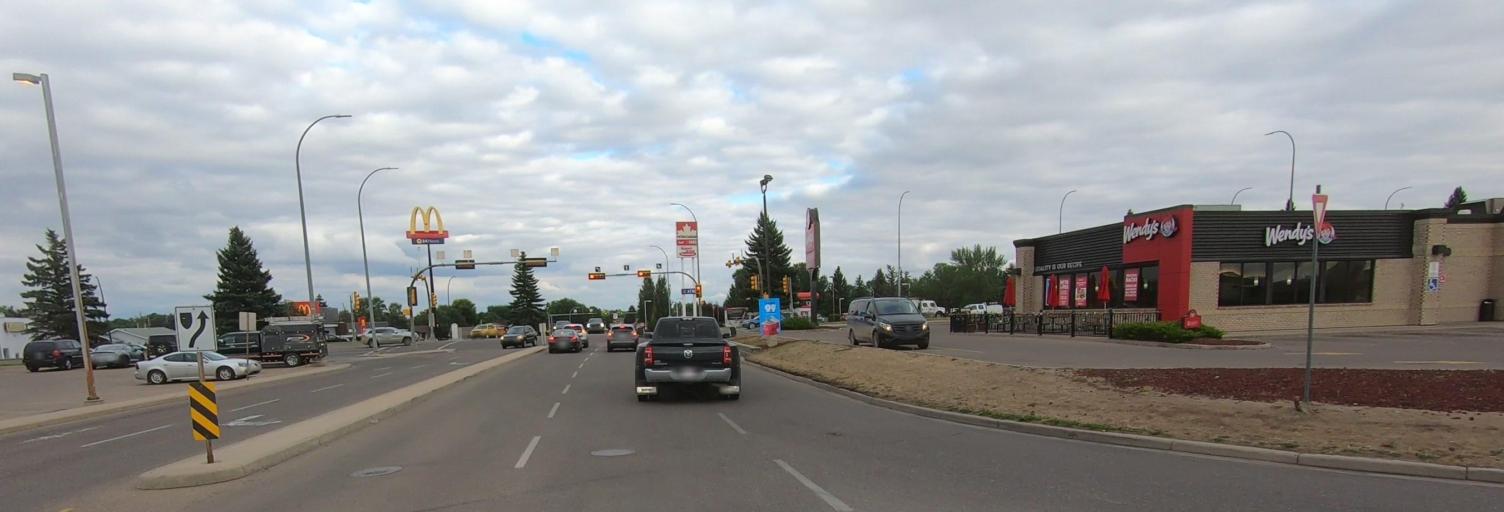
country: CA
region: Alberta
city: Medicine Hat
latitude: 50.0034
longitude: -110.6443
